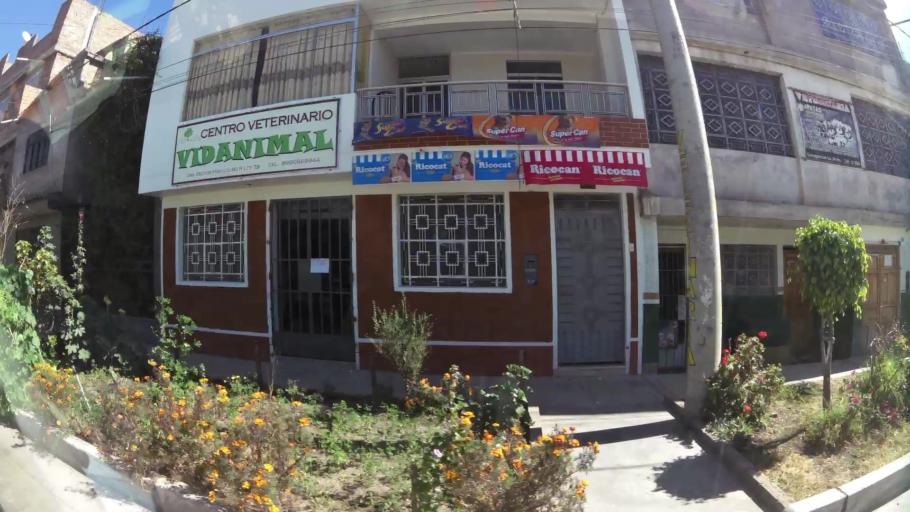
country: PE
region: Ayacucho
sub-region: Provincia de Huamanga
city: Ayacucho
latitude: -13.1469
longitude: -74.2278
